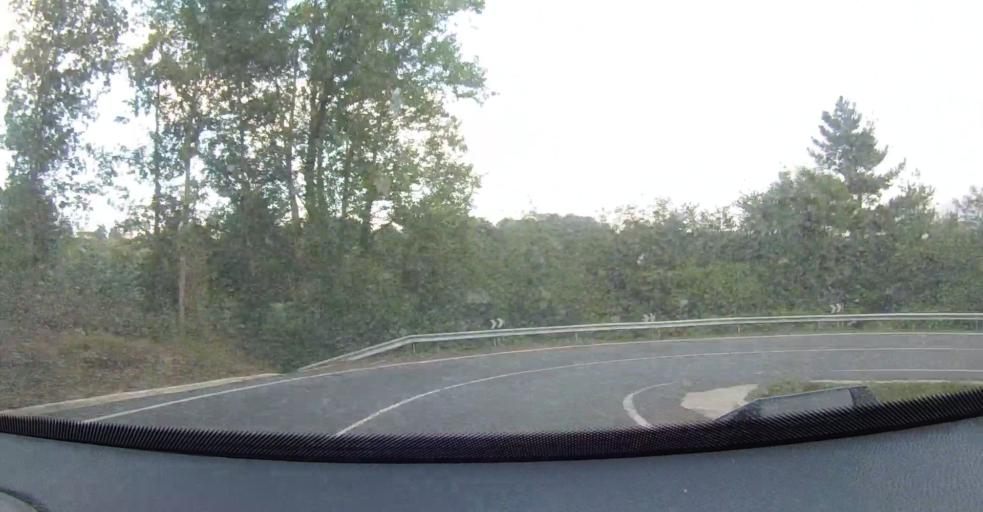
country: ES
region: Basque Country
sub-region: Bizkaia
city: Sopuerta
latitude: 43.2840
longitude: -3.1611
